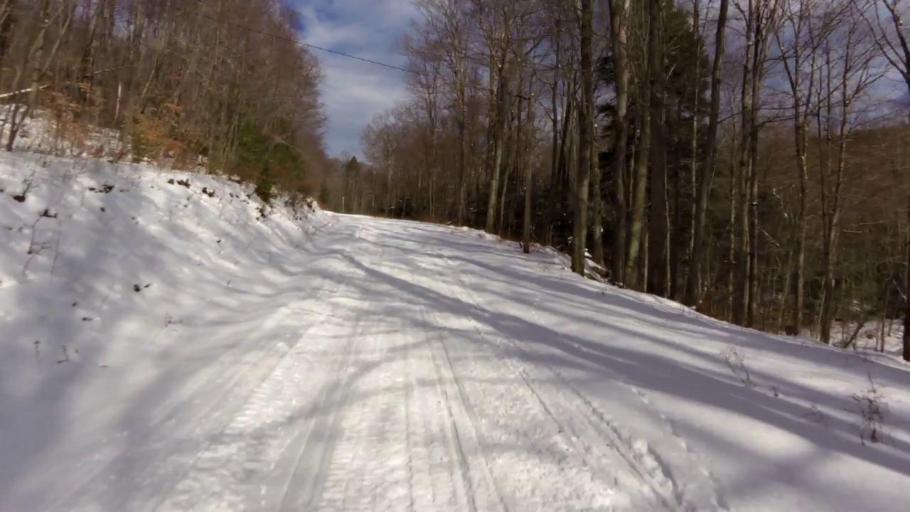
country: US
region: Pennsylvania
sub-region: McKean County
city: Foster Brook
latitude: 42.0069
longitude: -78.6022
